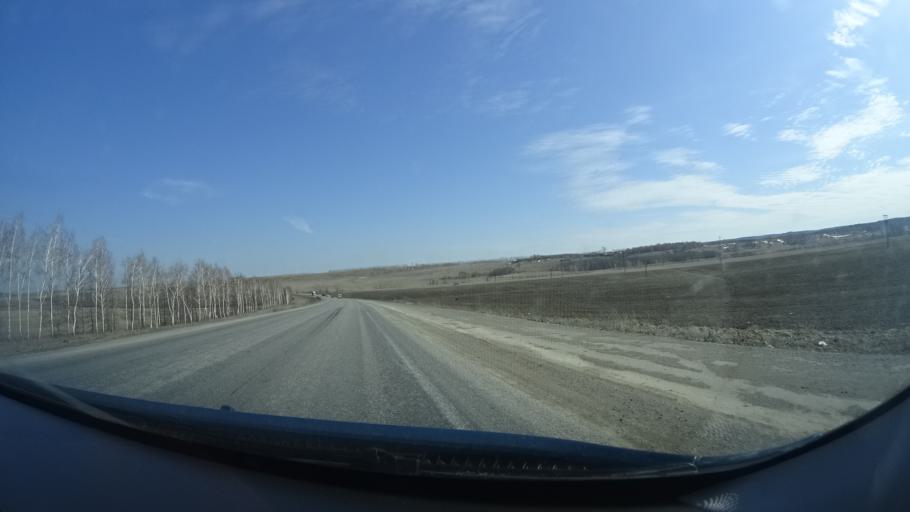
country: RU
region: Bashkortostan
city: Serafimovskiy
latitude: 54.4562
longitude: 53.7036
